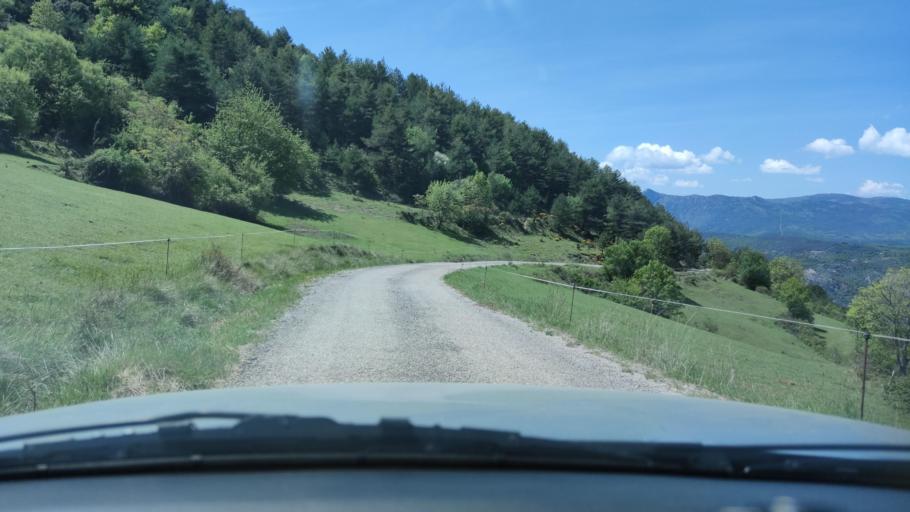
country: ES
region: Catalonia
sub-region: Provincia de Lleida
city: Sort
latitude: 42.3237
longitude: 1.0963
